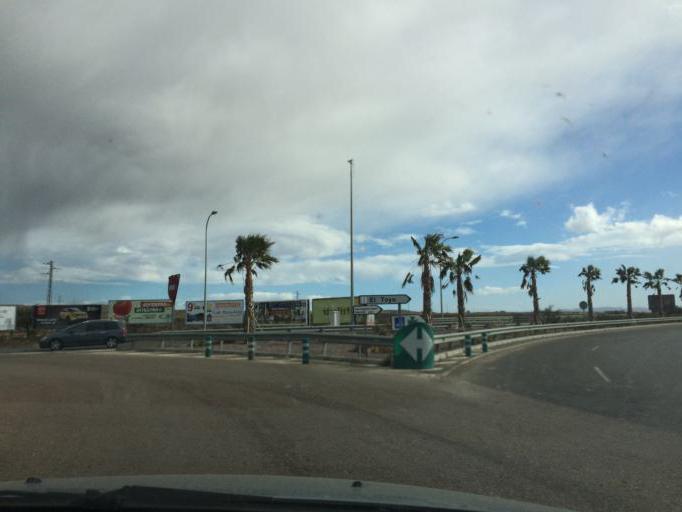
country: ES
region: Andalusia
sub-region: Provincia de Almeria
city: Retamar
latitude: 36.8547
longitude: -2.3448
